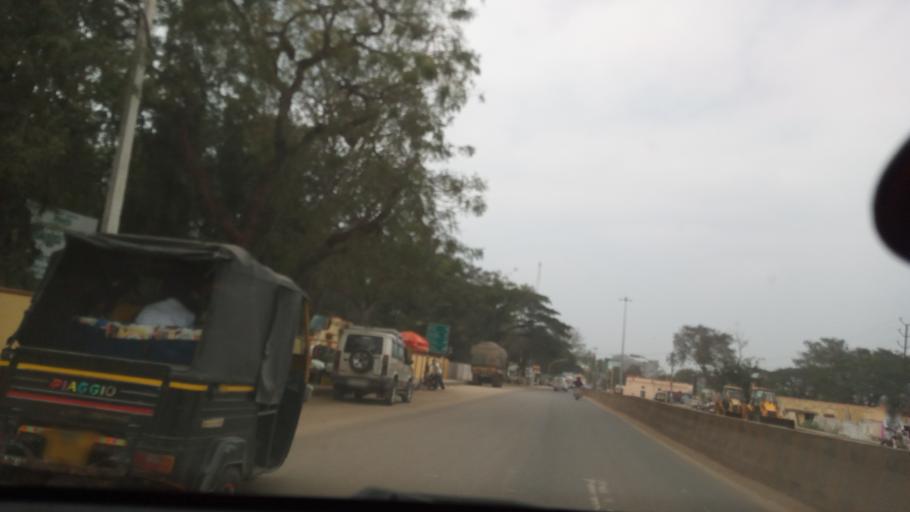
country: IN
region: Karnataka
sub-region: Chamrajnagar
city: Chamrajnagar
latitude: 11.9202
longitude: 76.9392
